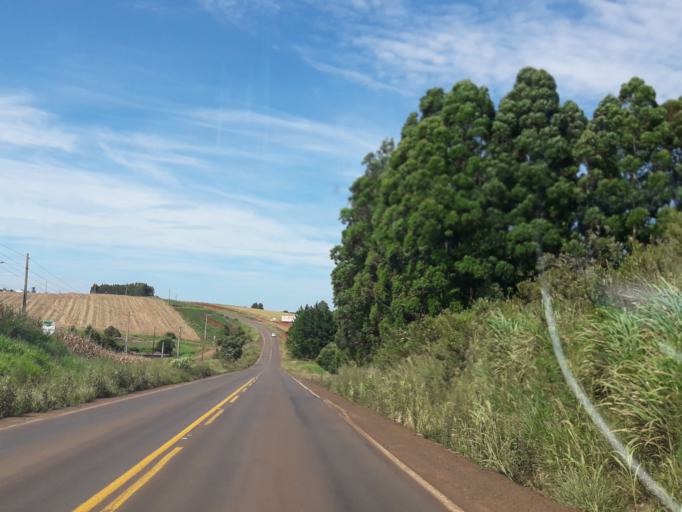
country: AR
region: Misiones
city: Bernardo de Irigoyen
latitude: -26.4152
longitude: -53.5246
